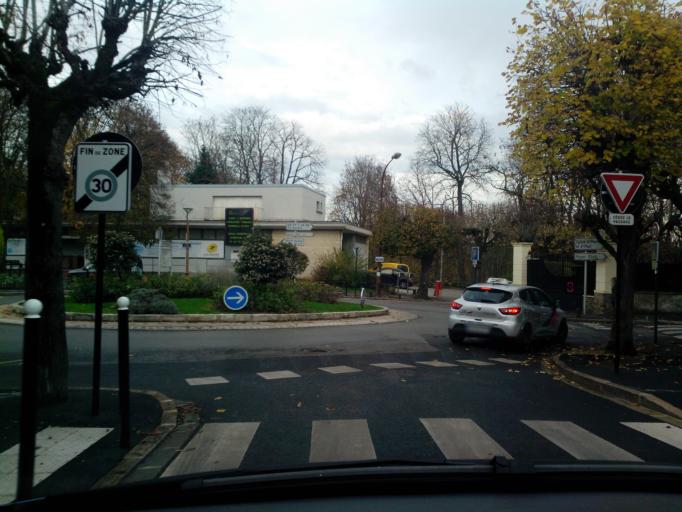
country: FR
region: Ile-de-France
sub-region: Departement de l'Essonne
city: Evry
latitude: 48.6357
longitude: 2.4468
